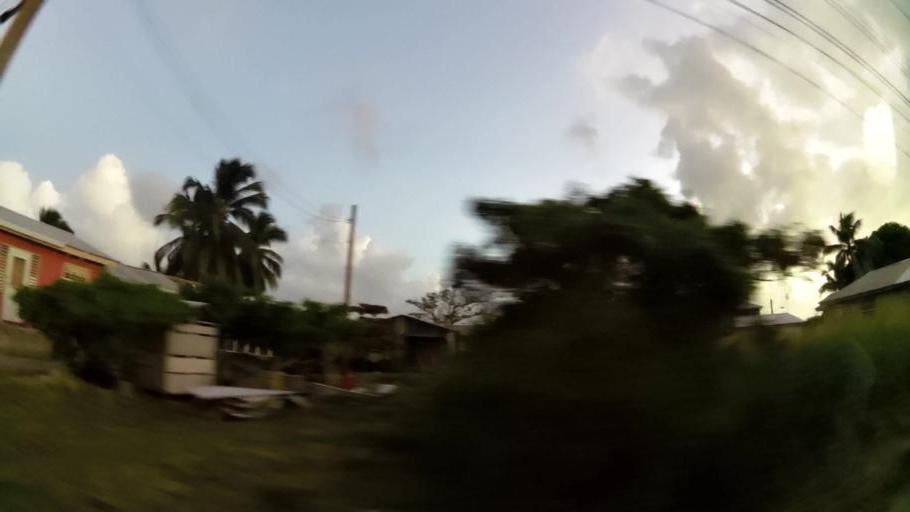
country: BB
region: Saint John
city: Four Cross Roads
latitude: 13.1173
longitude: -59.5234
